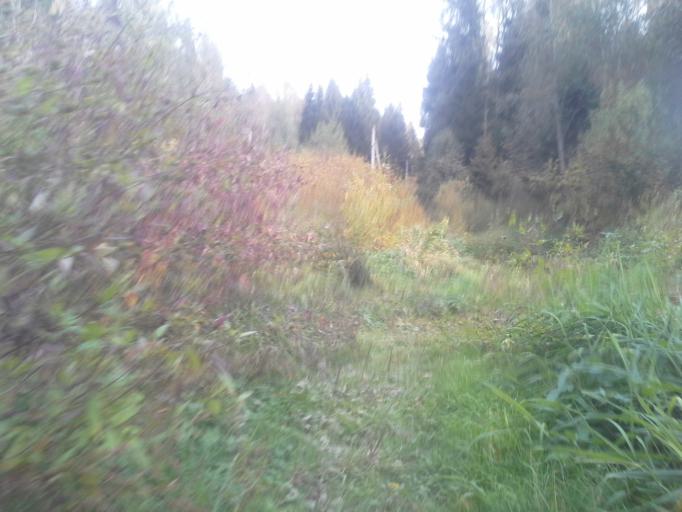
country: RU
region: Moskovskaya
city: Selyatino
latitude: 55.4562
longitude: 36.9705
